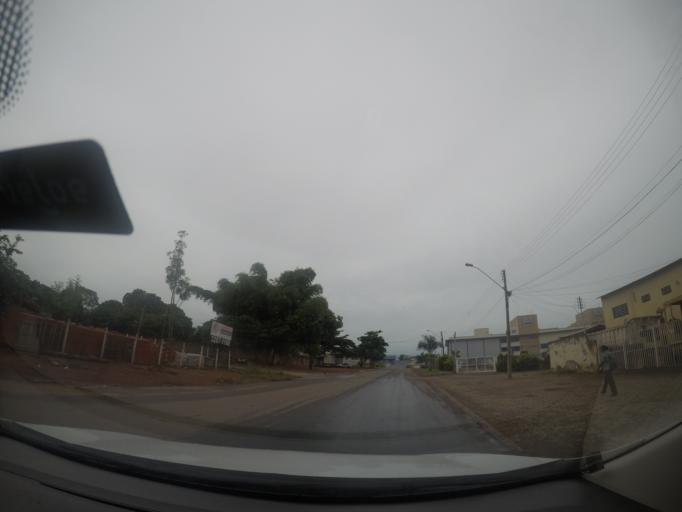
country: BR
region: Goias
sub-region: Goiania
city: Goiania
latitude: -16.6350
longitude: -49.2371
